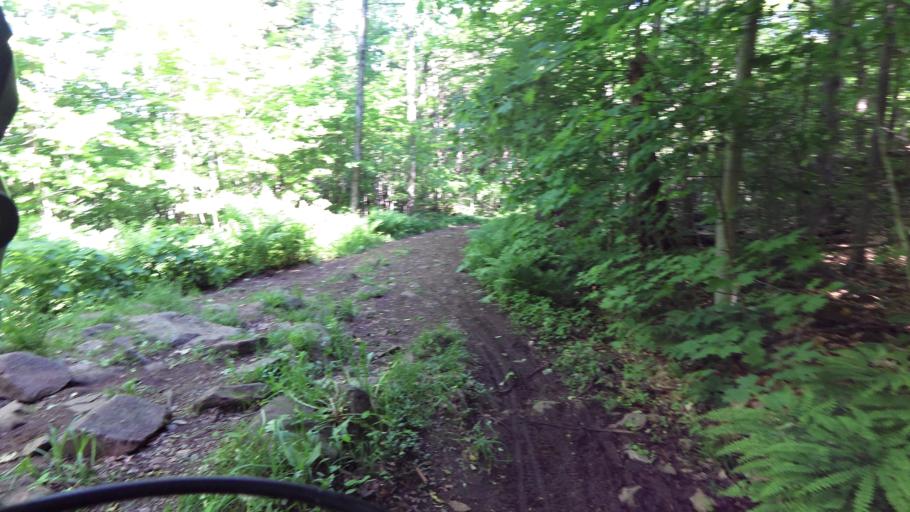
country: CA
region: Quebec
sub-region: Outaouais
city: Wakefield
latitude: 45.5387
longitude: -75.8759
